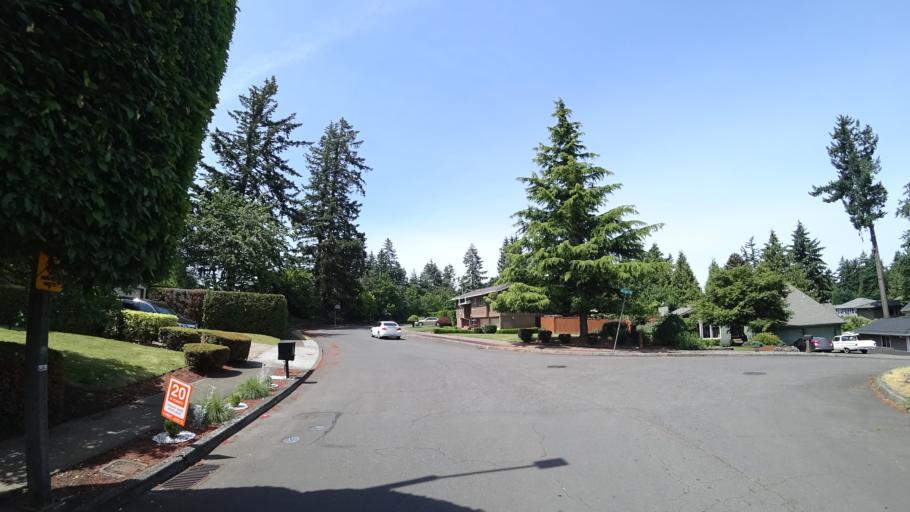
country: US
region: Oregon
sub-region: Multnomah County
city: Fairview
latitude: 45.5431
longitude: -122.5019
